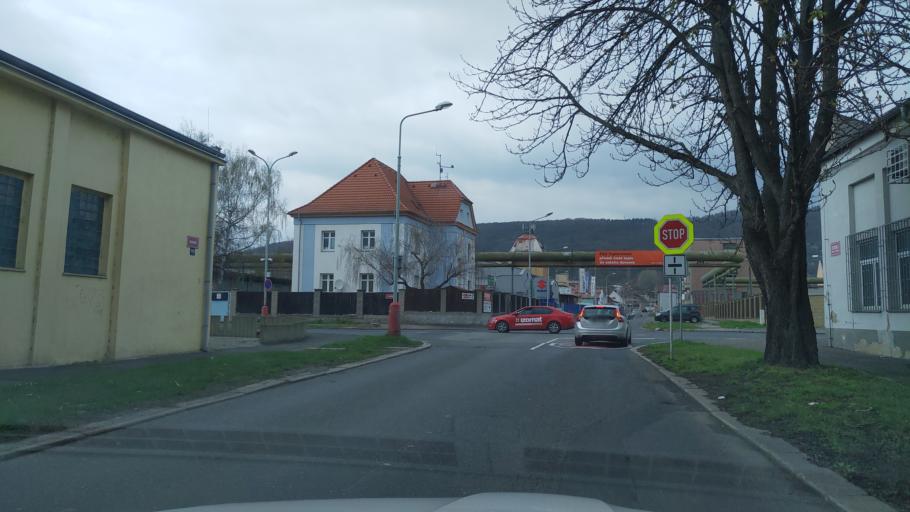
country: CZ
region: Ustecky
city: Trmice
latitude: 50.6586
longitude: 14.0039
